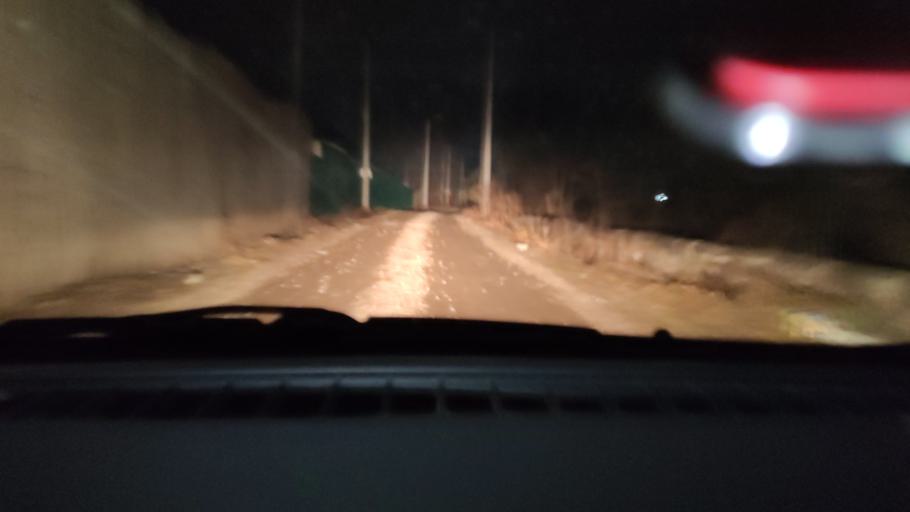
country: RU
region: Perm
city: Kondratovo
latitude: 58.0042
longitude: 56.0983
